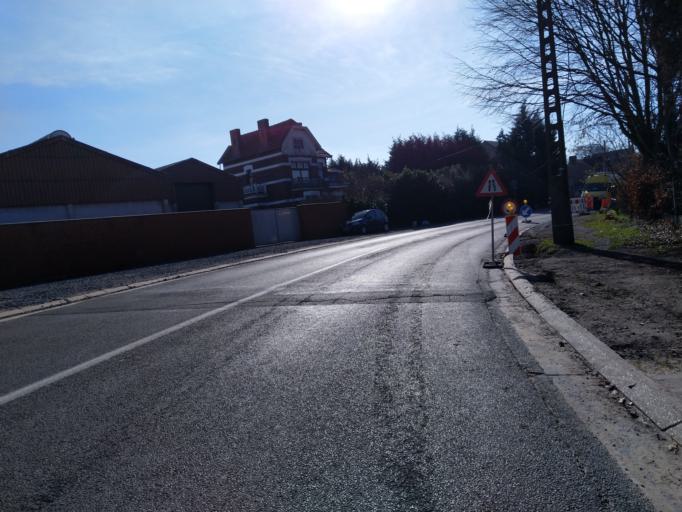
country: BE
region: Wallonia
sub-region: Province du Hainaut
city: Frameries
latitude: 50.3902
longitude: 3.8877
